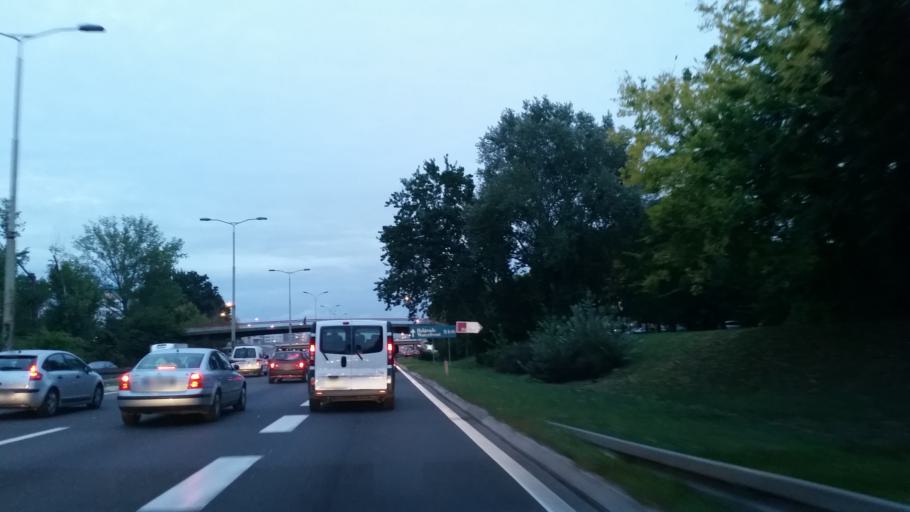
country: RS
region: Central Serbia
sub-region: Belgrade
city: Novi Beograd
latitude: 44.8150
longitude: 20.4146
